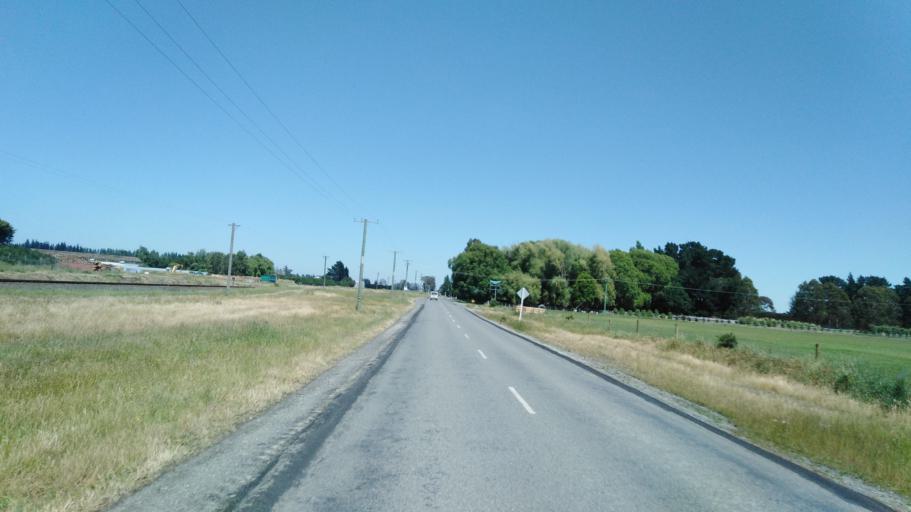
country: NZ
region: Canterbury
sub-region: Selwyn District
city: Rolleston
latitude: -43.5663
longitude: 172.4420
